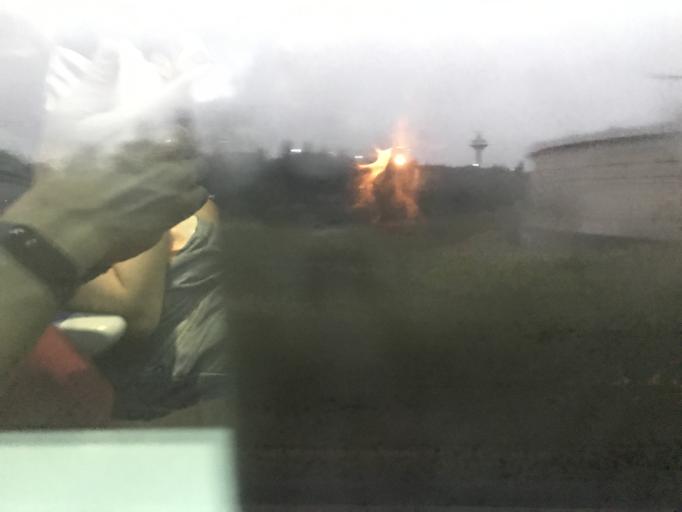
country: TR
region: Kocaeli
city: Korfez
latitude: 40.7471
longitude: 29.7821
